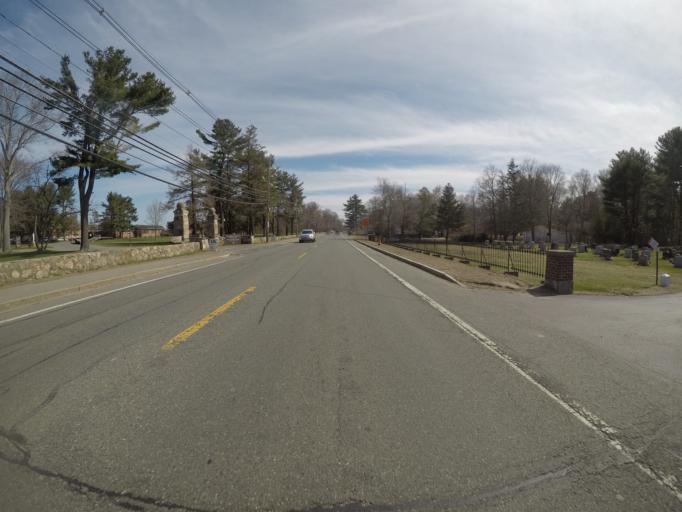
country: US
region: Massachusetts
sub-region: Bristol County
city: Easton
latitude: 42.0550
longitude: -71.0857
